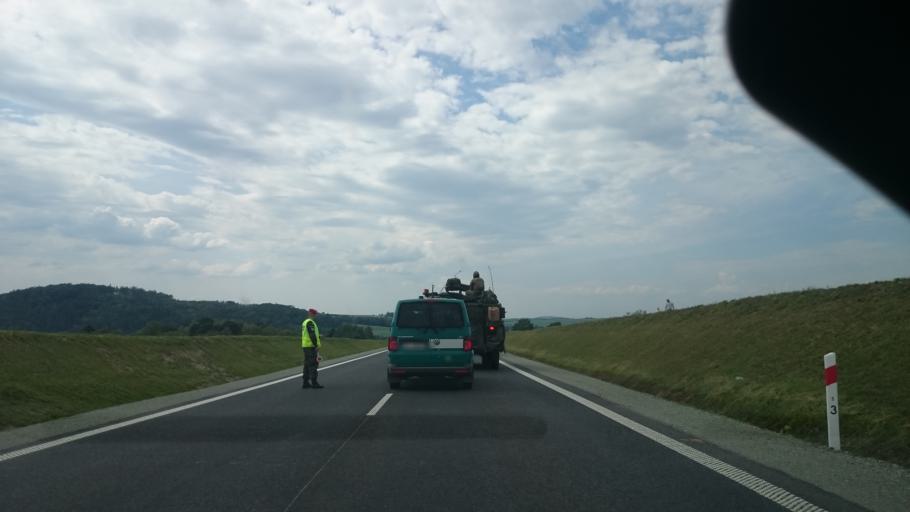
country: PL
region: Lower Silesian Voivodeship
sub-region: Powiat klodzki
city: Klodzko
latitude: 50.4004
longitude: 16.6498
